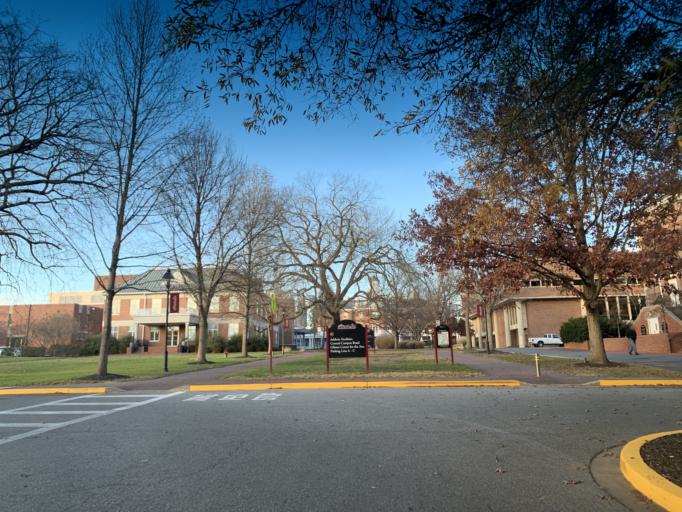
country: US
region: Maryland
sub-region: Kent County
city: Chestertown
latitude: 39.2165
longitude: -76.0690
